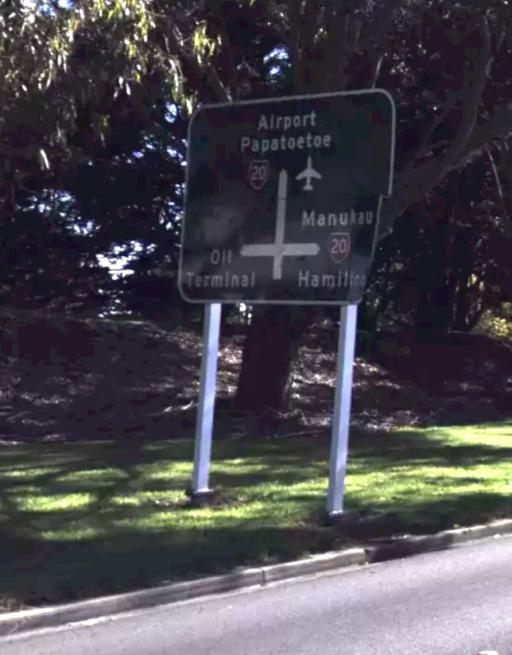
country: NZ
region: Auckland
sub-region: Auckland
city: Wiri
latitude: -37.0067
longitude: 174.8555
